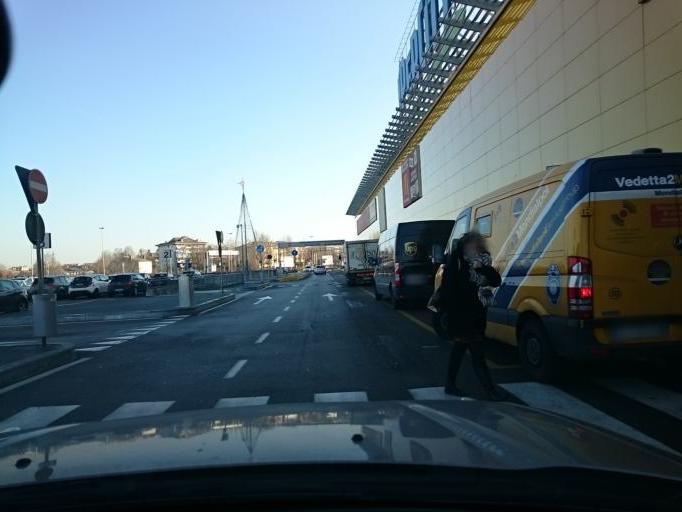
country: IT
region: Veneto
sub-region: Provincia di Padova
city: Mandriola-Sant'Agostino
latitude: 45.3785
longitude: 11.8546
